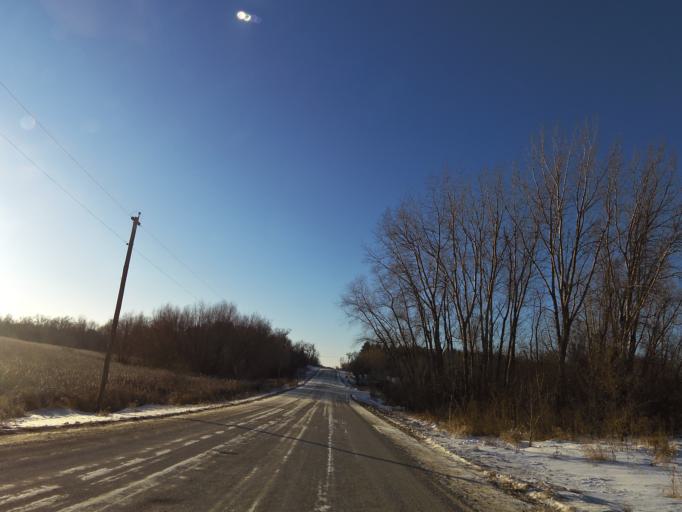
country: US
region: Minnesota
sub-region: Le Sueur County
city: New Prague
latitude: 44.6387
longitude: -93.5166
